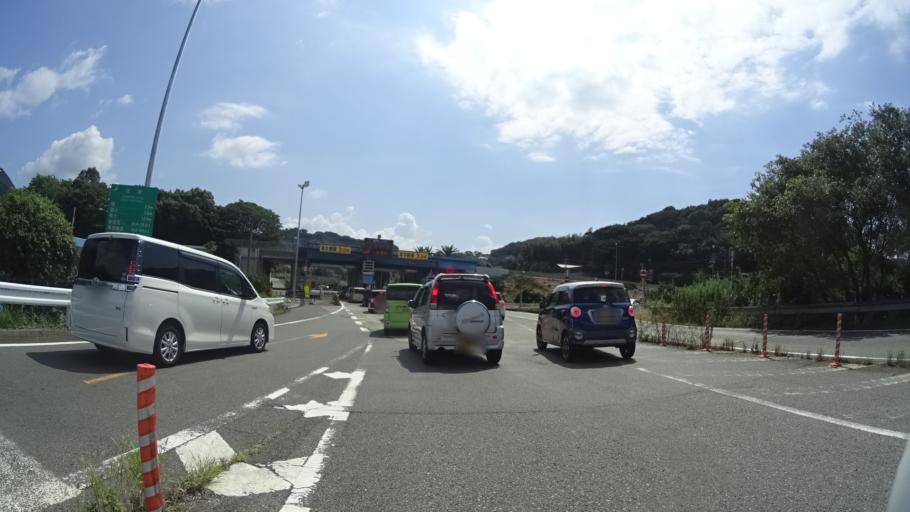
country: JP
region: Yamaguchi
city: Shimonoseki
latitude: 33.9779
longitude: 130.9465
